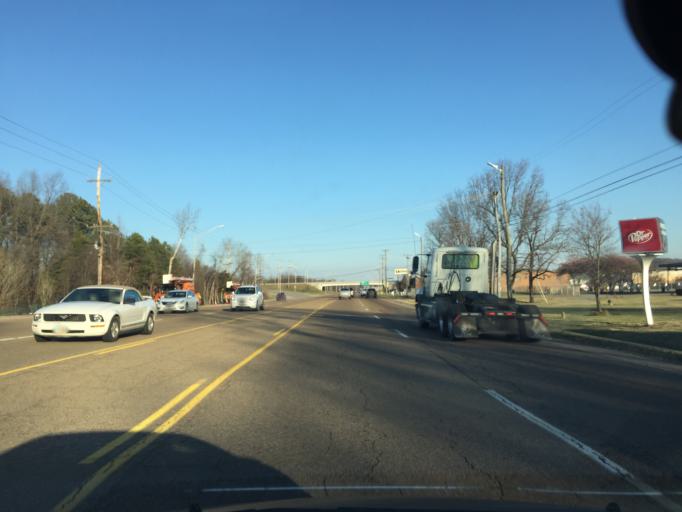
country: US
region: Tennessee
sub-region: Hamilton County
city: East Chattanooga
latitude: 35.0937
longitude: -85.2541
